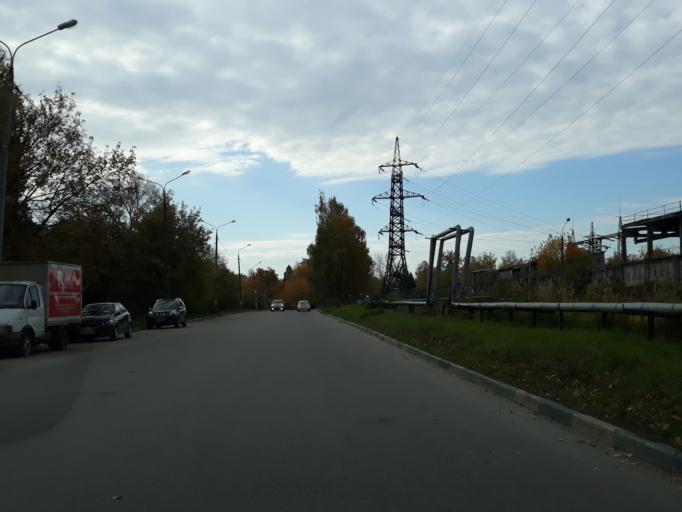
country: RU
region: Nizjnij Novgorod
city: Nizhniy Novgorod
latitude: 56.2392
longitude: 43.9780
